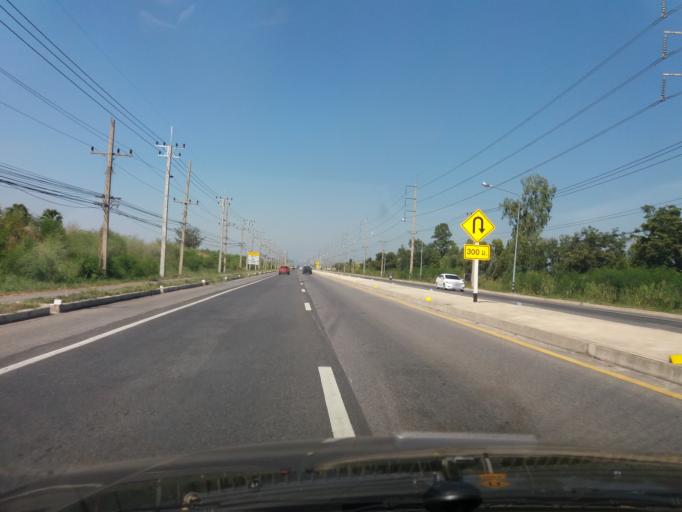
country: TH
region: Chai Nat
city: Manorom
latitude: 15.2936
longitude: 100.0987
